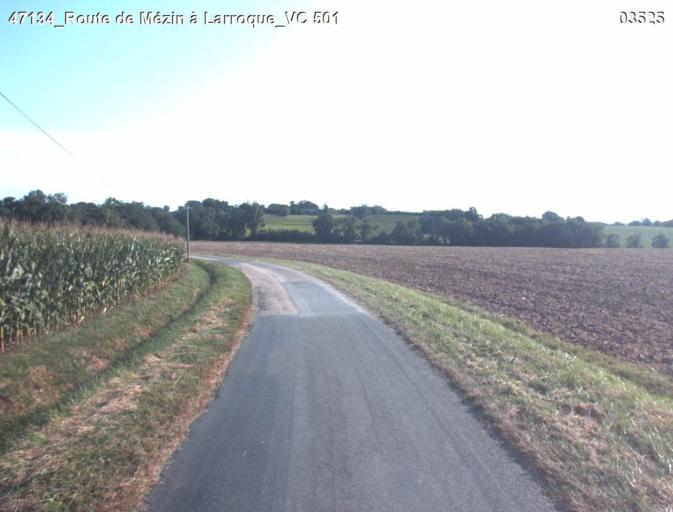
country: FR
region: Aquitaine
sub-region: Departement du Lot-et-Garonne
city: Mezin
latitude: 44.0263
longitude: 0.2690
